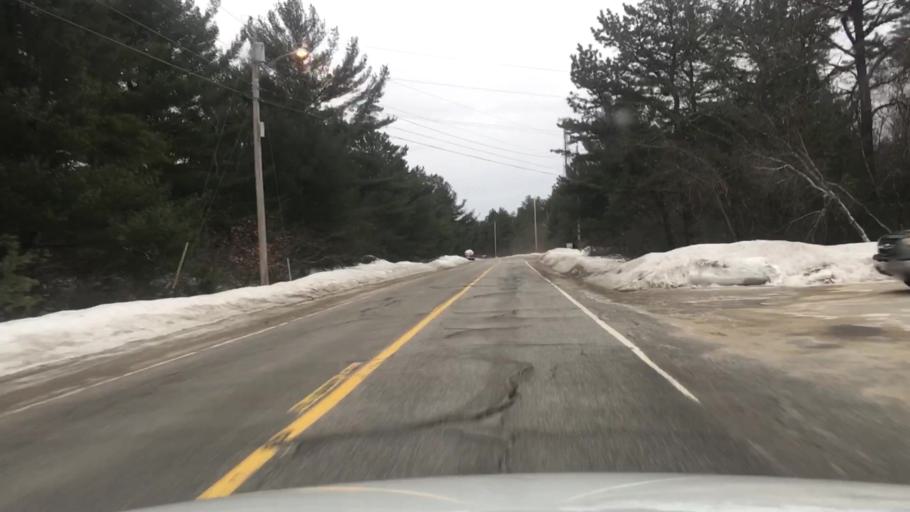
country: US
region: Maine
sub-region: York County
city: Shapleigh
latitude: 43.5714
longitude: -70.8619
